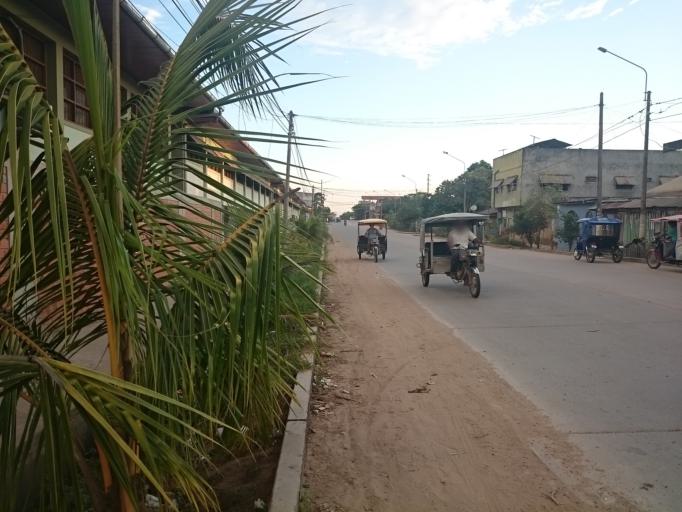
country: PE
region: Ucayali
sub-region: Provincia de Coronel Portillo
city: Pucallpa
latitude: -8.3733
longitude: -74.5350
